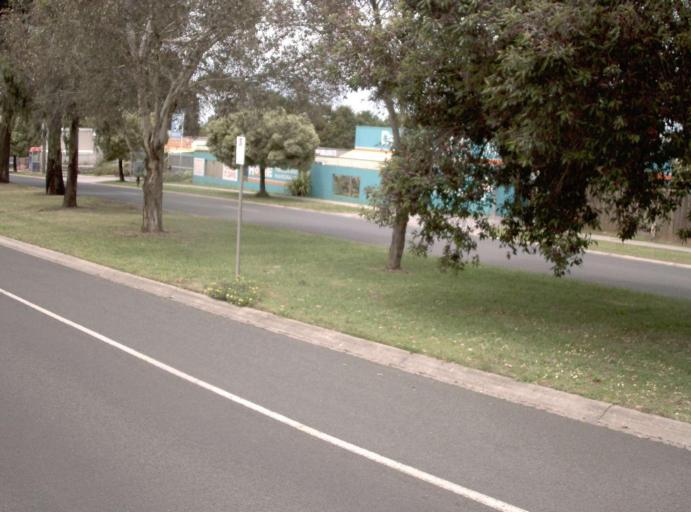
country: AU
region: Victoria
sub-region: Baw Baw
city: Warragul
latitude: -38.1188
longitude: 145.8422
